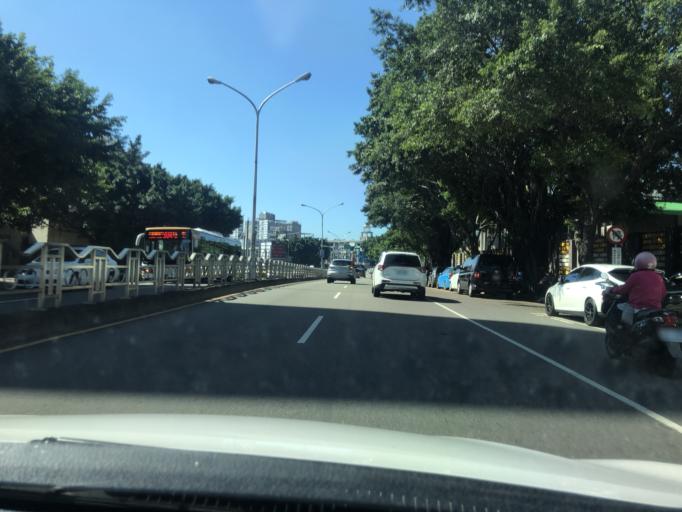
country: TW
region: Taiwan
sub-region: Taichung City
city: Taichung
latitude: 24.1571
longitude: 120.6852
